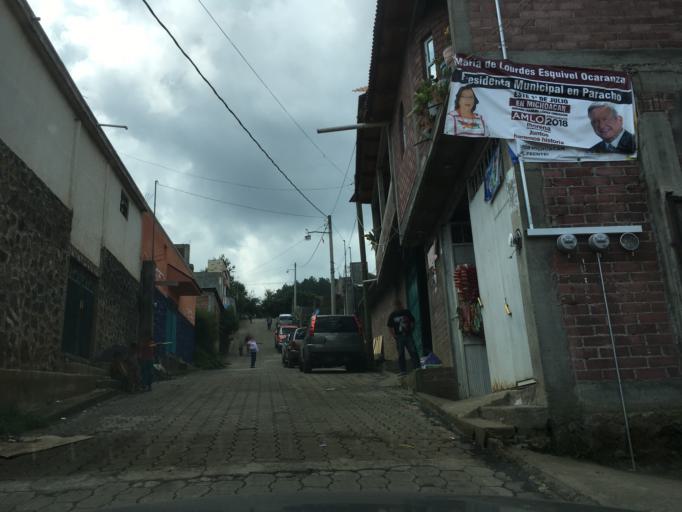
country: MX
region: Michoacan
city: Capacuaro
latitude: 19.5957
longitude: -102.0014
